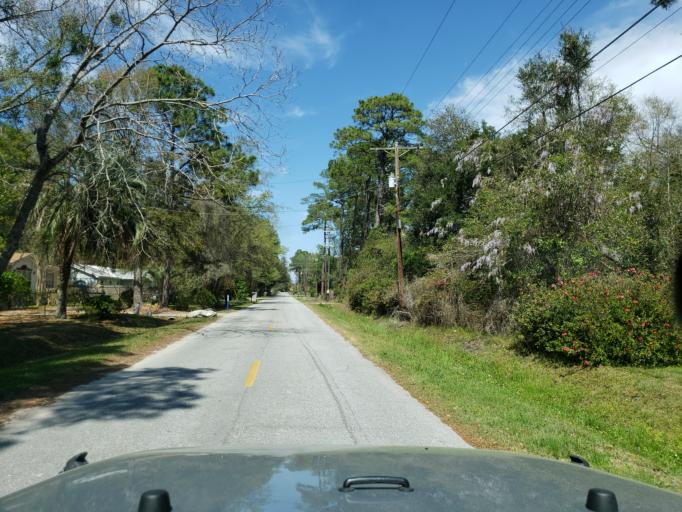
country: US
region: Georgia
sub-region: Chatham County
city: Montgomery
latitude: 31.9500
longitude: -81.1136
